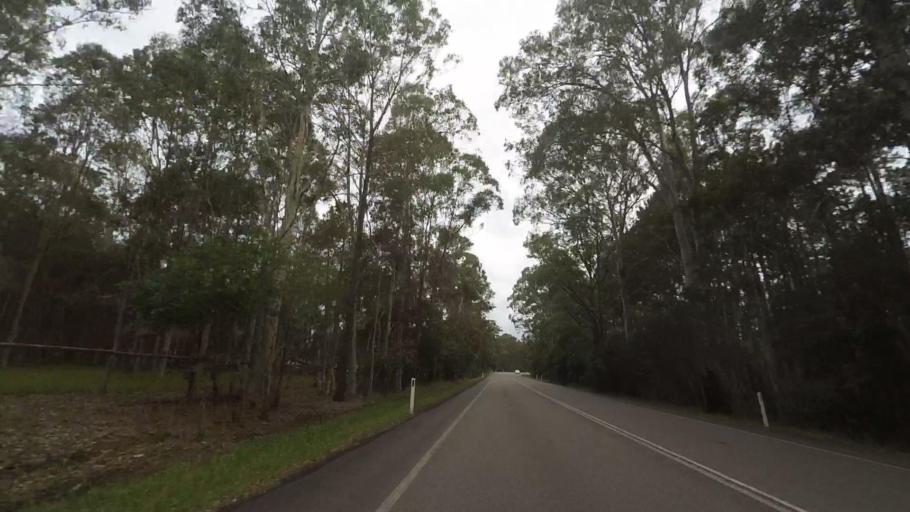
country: AU
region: New South Wales
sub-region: Great Lakes
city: Hawks Nest
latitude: -32.6212
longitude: 152.1238
